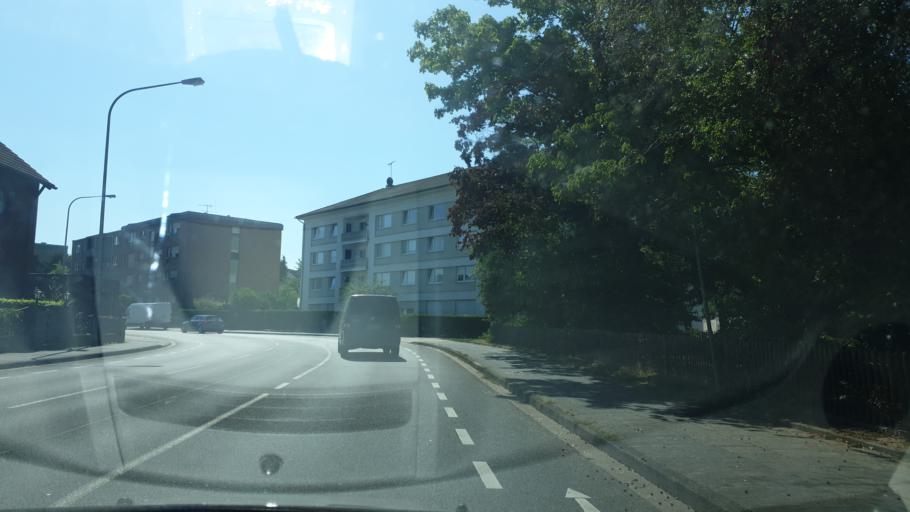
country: DE
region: North Rhine-Westphalia
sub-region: Regierungsbezirk Koln
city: Euskirchen
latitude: 50.6639
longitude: 6.7739
